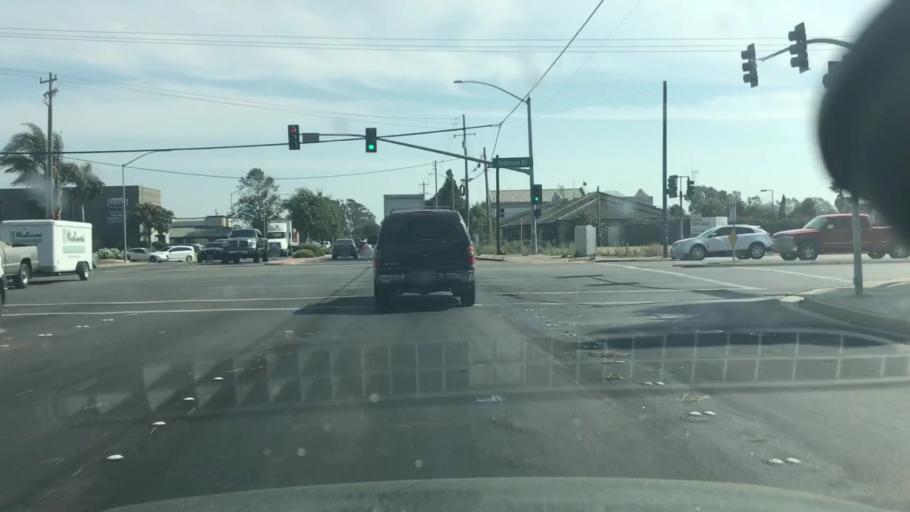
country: US
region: California
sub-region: Santa Barbara County
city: Santa Maria
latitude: 34.9211
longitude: -120.4541
